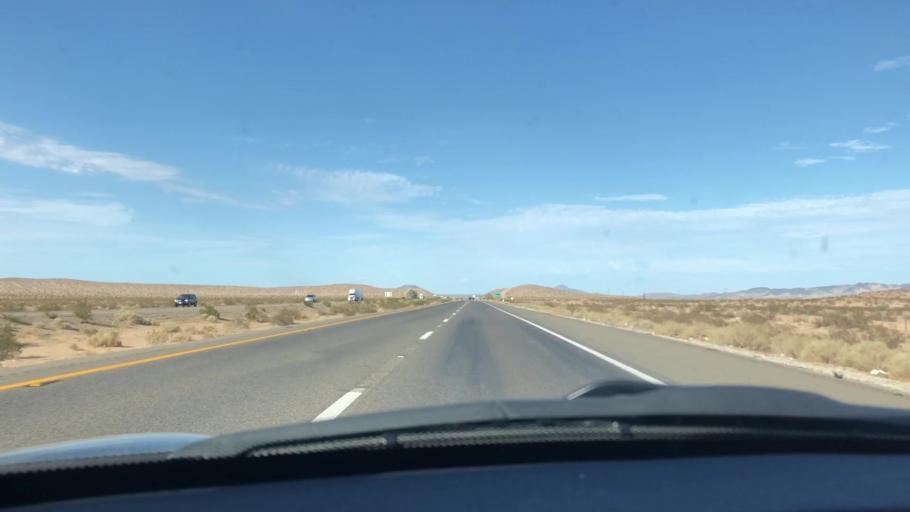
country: US
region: California
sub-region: San Bernardino County
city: Fort Irwin
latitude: 34.9666
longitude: -116.6376
